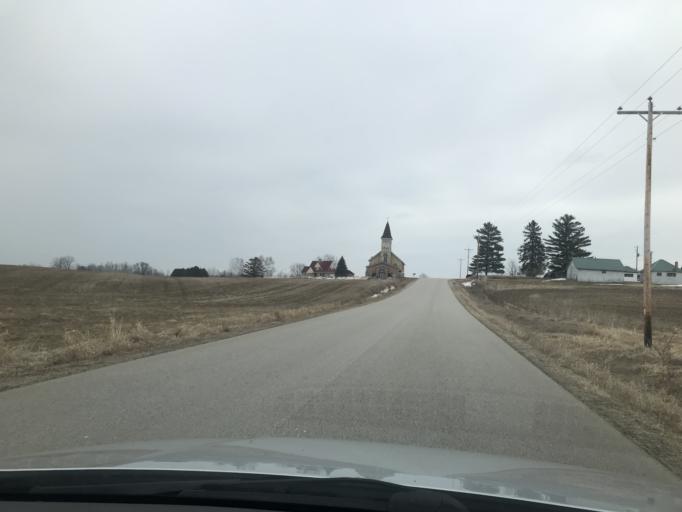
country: US
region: Wisconsin
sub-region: Marinette County
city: Peshtigo
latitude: 45.0272
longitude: -87.8733
